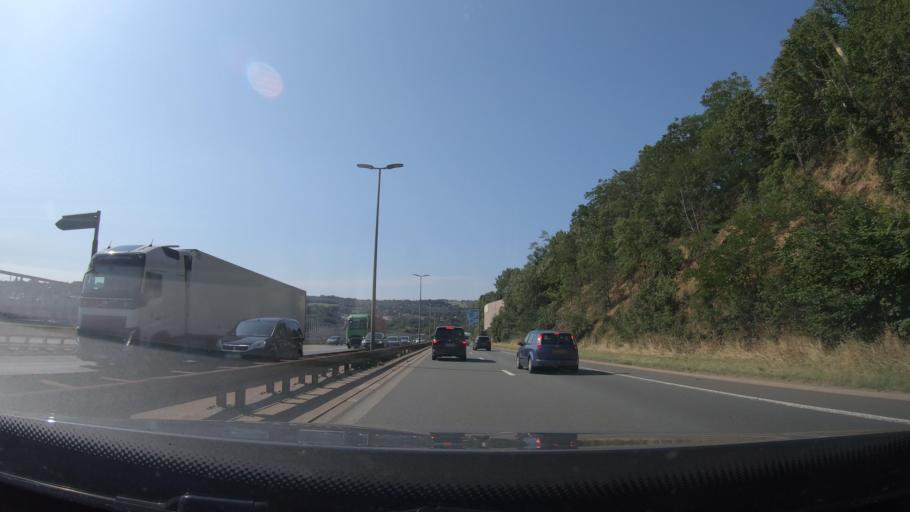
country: BE
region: Wallonia
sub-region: Province de Liege
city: Verviers
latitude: 50.5916
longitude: 5.8441
